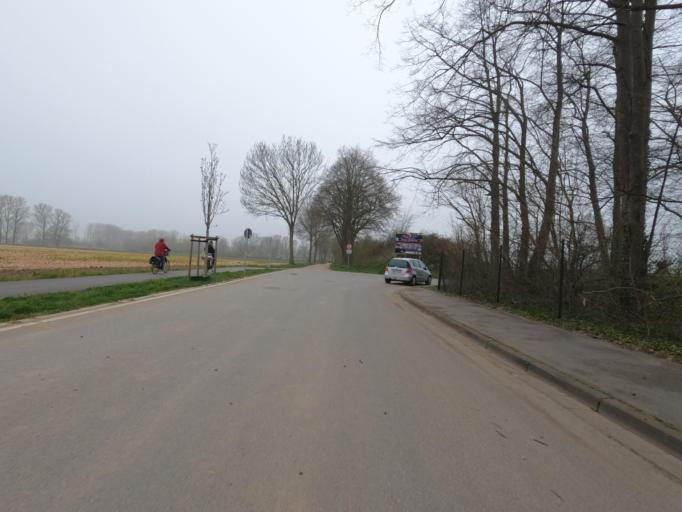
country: NL
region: Limburg
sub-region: Gemeente Roerdalen
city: Vlodrop
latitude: 51.1296
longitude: 6.0932
